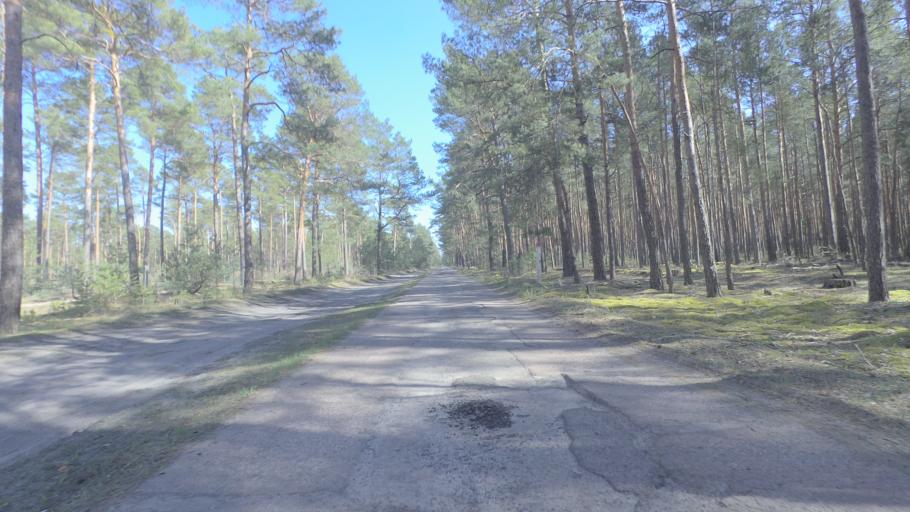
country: DE
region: Brandenburg
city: Halbe
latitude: 52.1745
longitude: 13.7382
